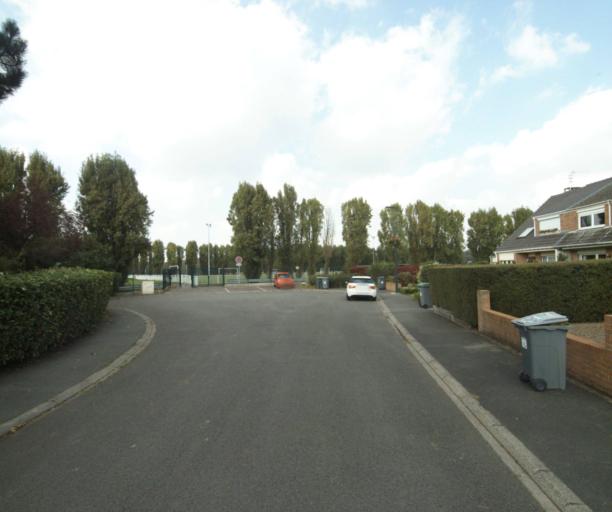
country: FR
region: Nord-Pas-de-Calais
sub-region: Departement du Nord
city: Houplin-Ancoisne
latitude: 50.5785
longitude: 3.0122
